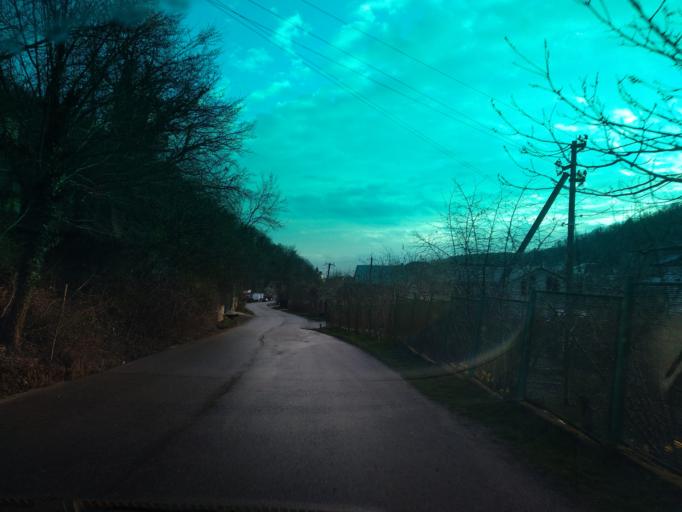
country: RU
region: Krasnodarskiy
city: Novomikhaylovskiy
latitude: 44.2692
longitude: 38.8301
